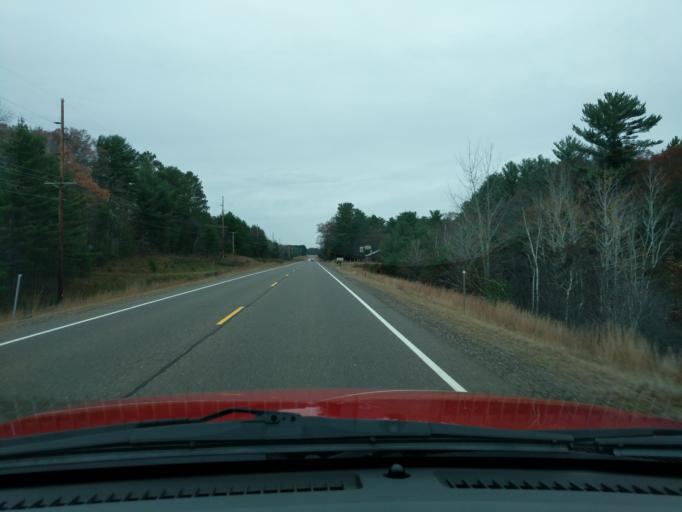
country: US
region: Wisconsin
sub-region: Burnett County
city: Siren
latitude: 45.8104
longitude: -92.2228
